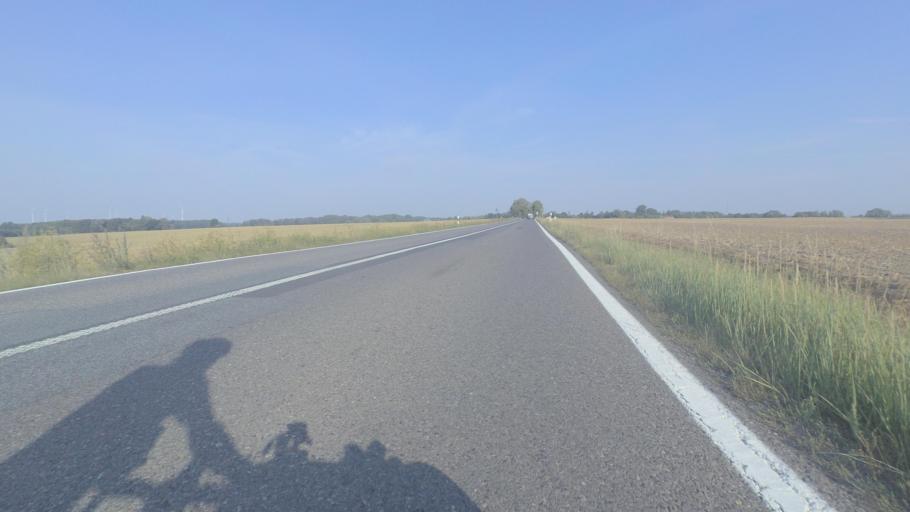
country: DE
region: Mecklenburg-Vorpommern
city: Grimmen
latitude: 54.0783
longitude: 13.1087
